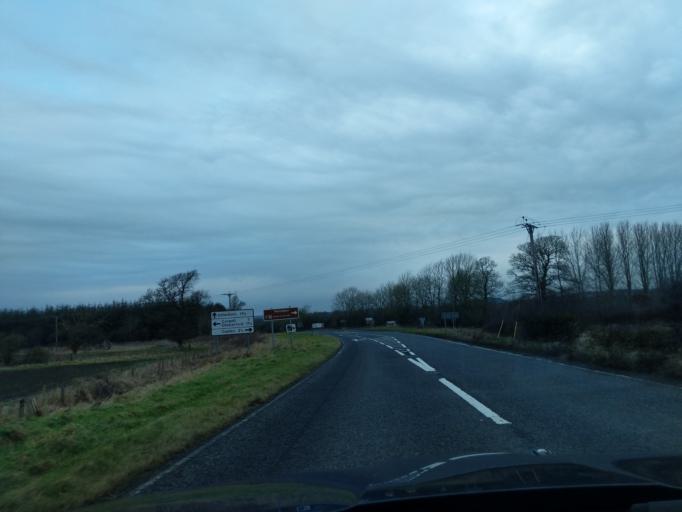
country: GB
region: England
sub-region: Northumberland
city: Rothley
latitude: 55.1364
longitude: -1.9669
